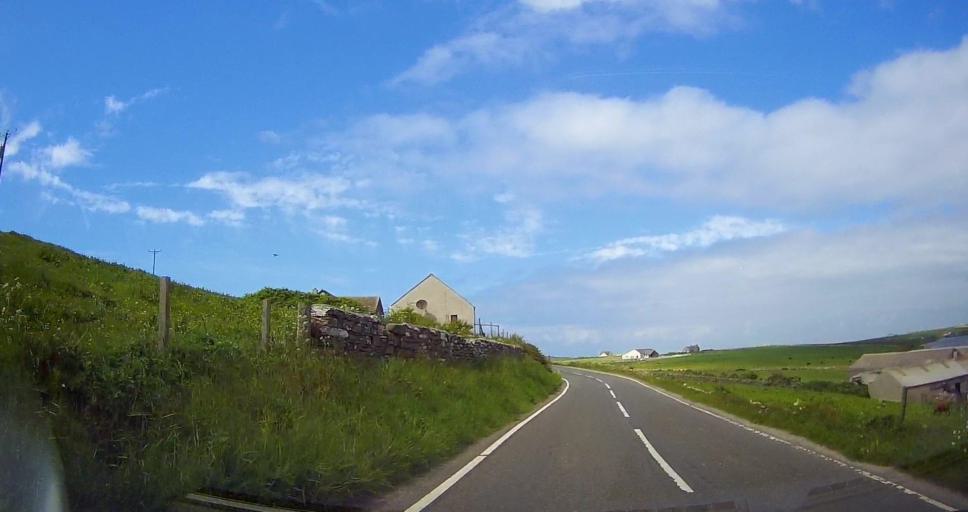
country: GB
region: Scotland
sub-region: Orkney Islands
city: Stromness
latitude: 59.1154
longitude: -3.3023
